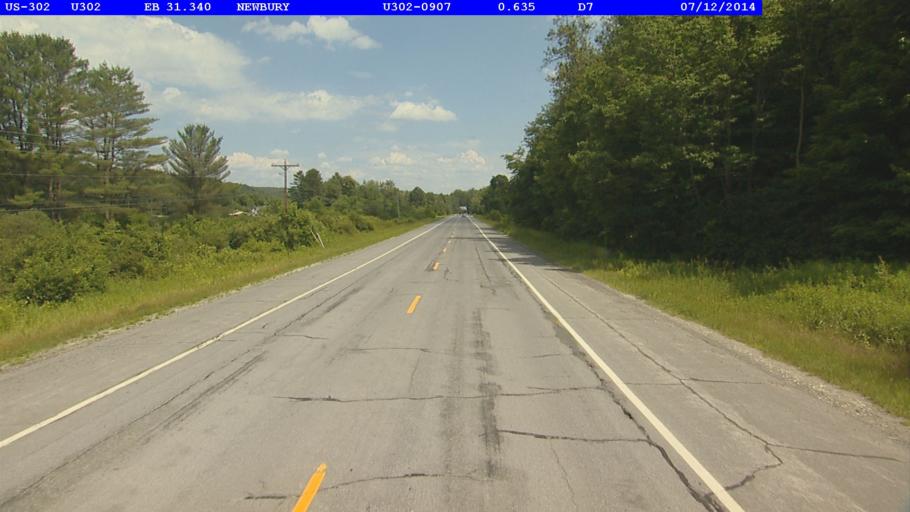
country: US
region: New Hampshire
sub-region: Grafton County
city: Woodsville
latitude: 44.1712
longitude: -72.1067
